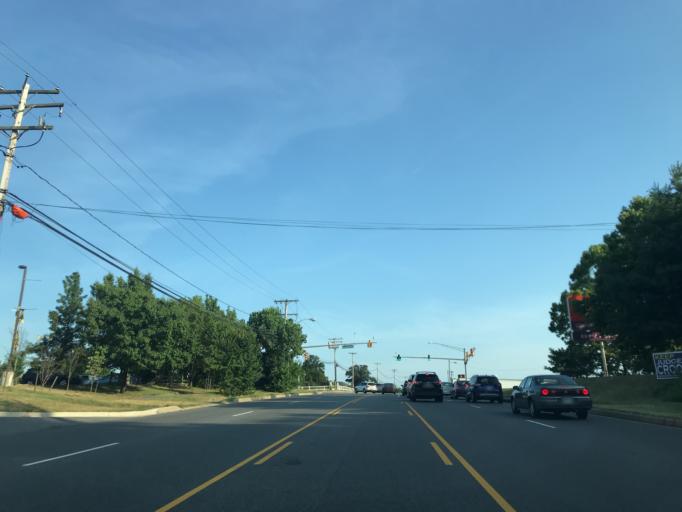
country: US
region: Maryland
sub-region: Anne Arundel County
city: South Gate
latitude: 39.1041
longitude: -76.6276
